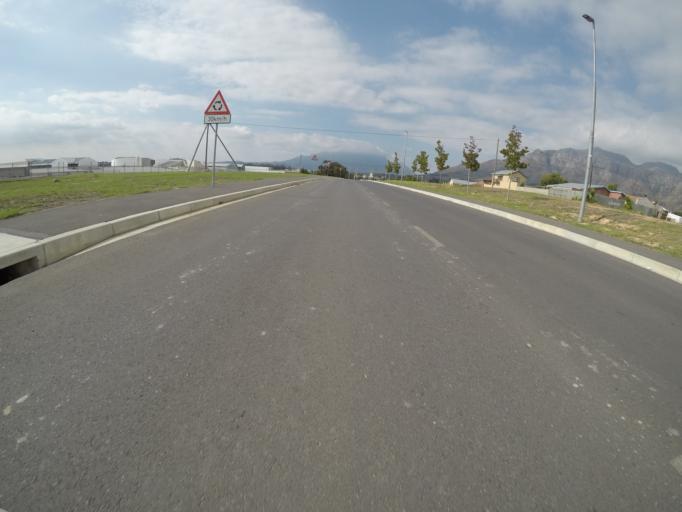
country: ZA
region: Western Cape
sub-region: Cape Winelands District Municipality
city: Stellenbosch
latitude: -33.9792
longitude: 18.8423
